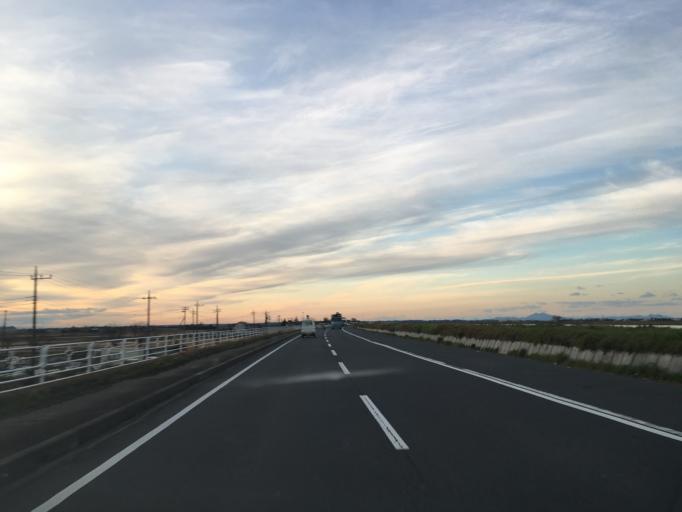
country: JP
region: Chiba
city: Katori-shi
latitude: 35.9078
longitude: 140.4829
